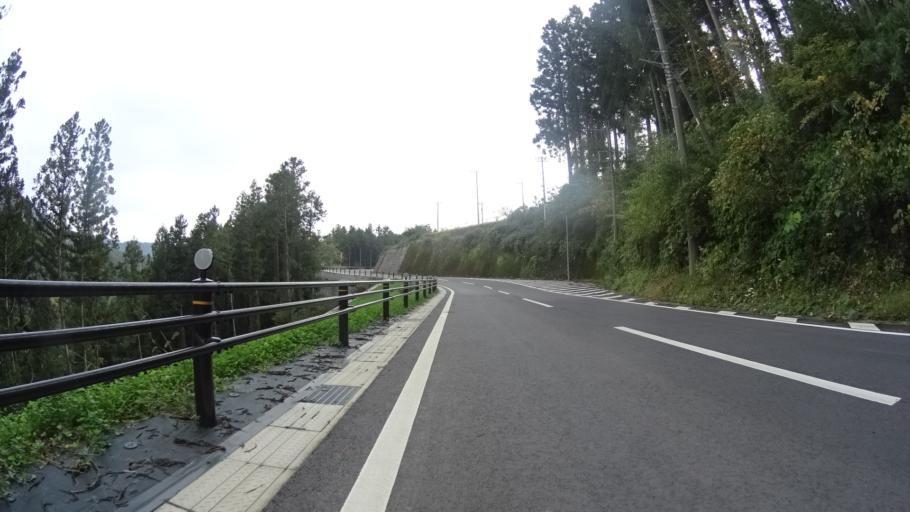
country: JP
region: Yamanashi
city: Uenohara
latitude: 35.6346
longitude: 139.0592
